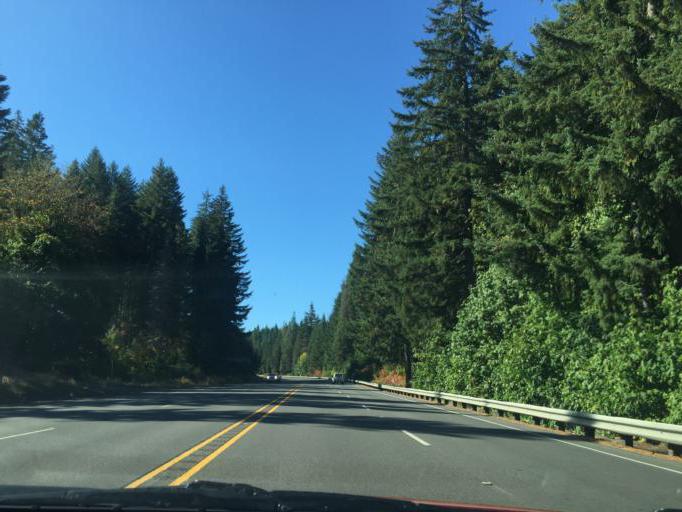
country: US
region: Oregon
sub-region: Columbia County
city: Vernonia
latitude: 45.7783
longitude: -123.3604
